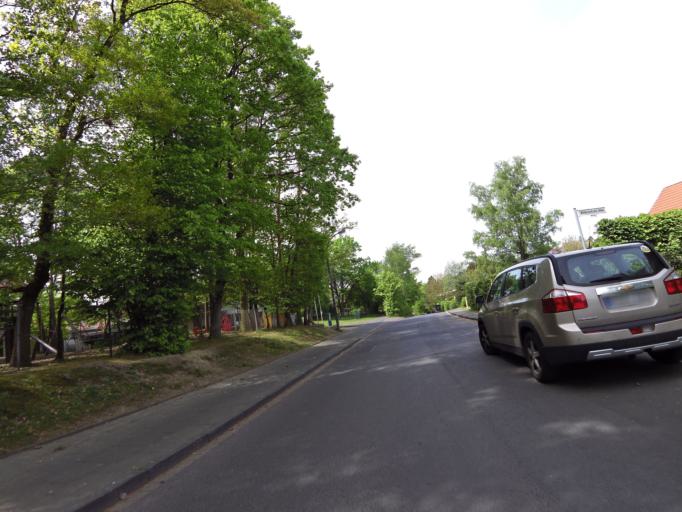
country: DE
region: North Rhine-Westphalia
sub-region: Regierungsbezirk Koln
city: Alfter
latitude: 50.6925
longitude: 7.0323
